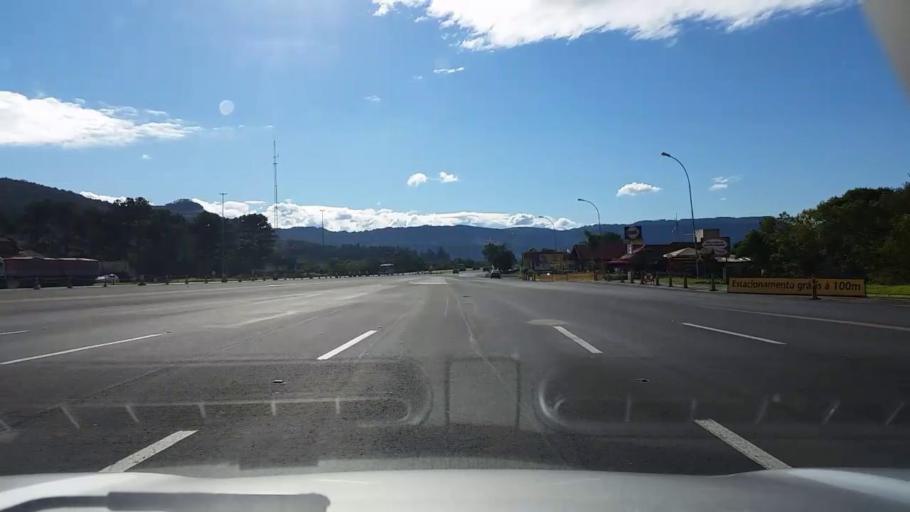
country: BR
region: Rio Grande do Sul
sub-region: Osorio
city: Osorio
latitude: -29.8852
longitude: -50.4466
